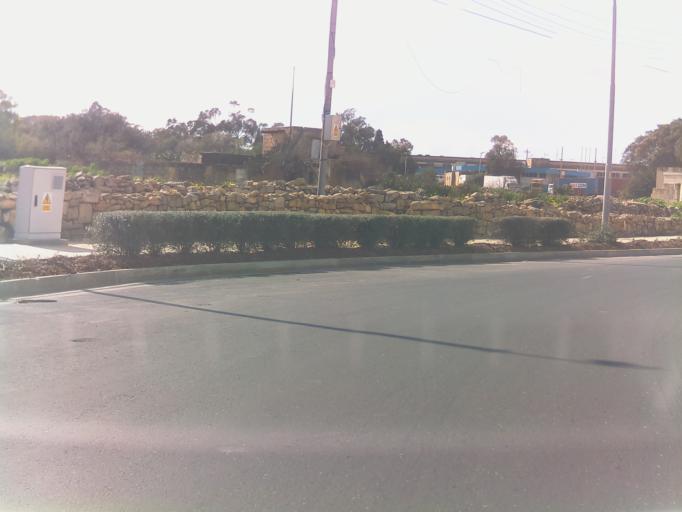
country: MT
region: Luqa
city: Luqa
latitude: 35.8558
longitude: 14.4892
